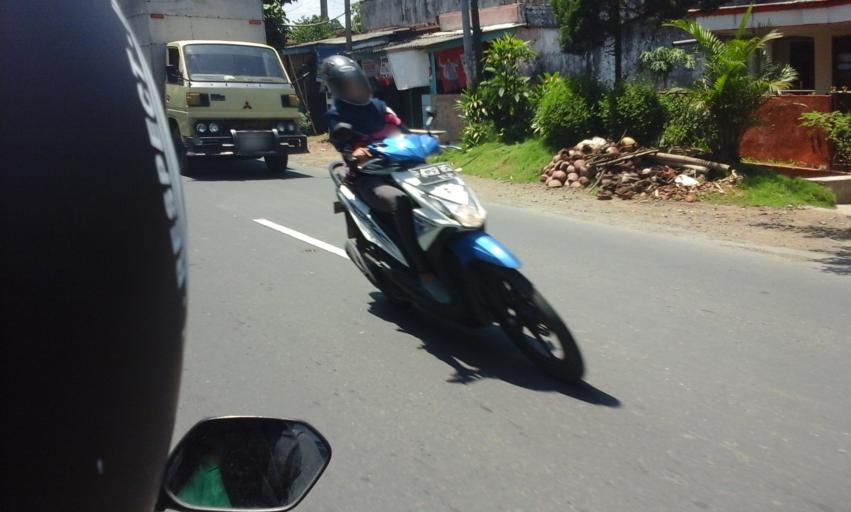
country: ID
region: East Java
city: Sumberdangdang
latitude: -8.1922
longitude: 113.7117
